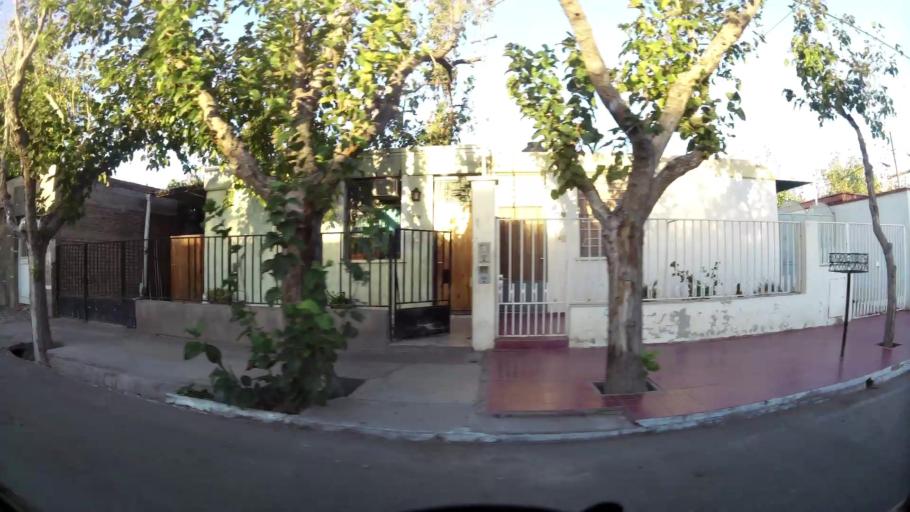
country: AR
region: San Juan
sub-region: Departamento de Santa Lucia
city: Santa Lucia
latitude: -31.5272
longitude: -68.5076
